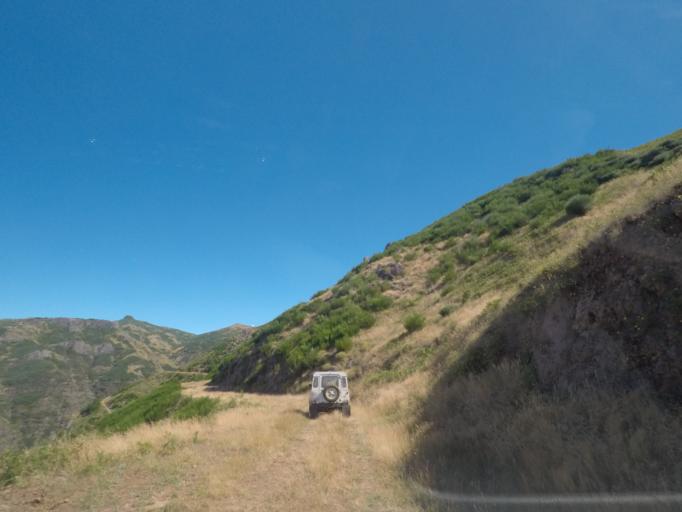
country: PT
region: Madeira
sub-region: Funchal
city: Nossa Senhora do Monte
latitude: 32.7046
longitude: -16.9159
